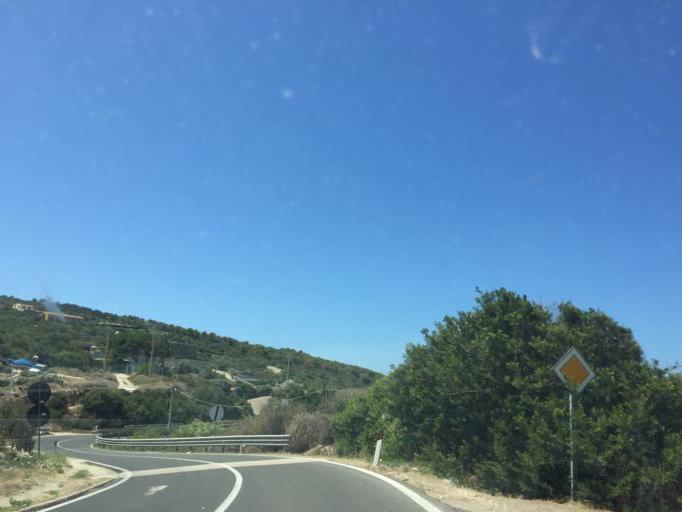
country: IT
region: Sardinia
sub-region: Provincia di Sassari
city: Castelsardo
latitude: 40.9112
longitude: 8.7341
